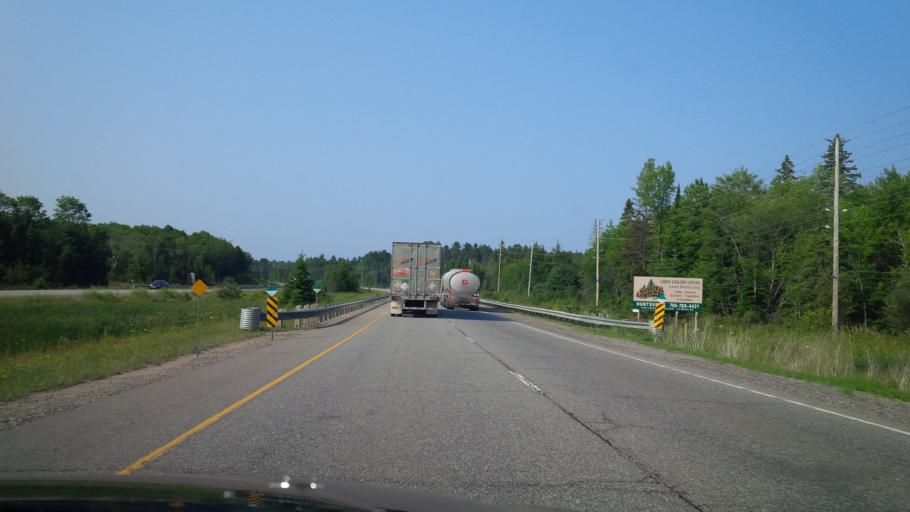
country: CA
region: Ontario
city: Huntsville
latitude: 45.2646
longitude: -79.2917
